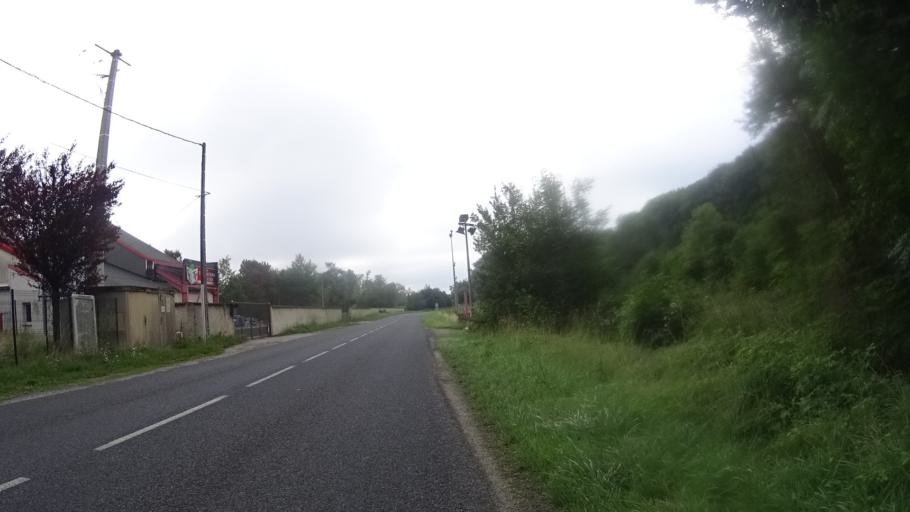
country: FR
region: Lorraine
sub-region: Departement de la Meuse
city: Fains-Veel
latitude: 48.8039
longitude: 5.1056
